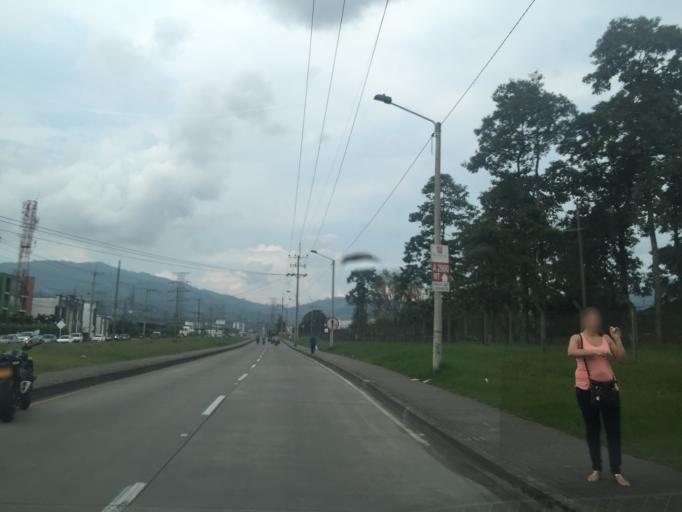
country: CO
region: Risaralda
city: Dos Quebradas
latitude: 4.8320
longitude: -75.6802
